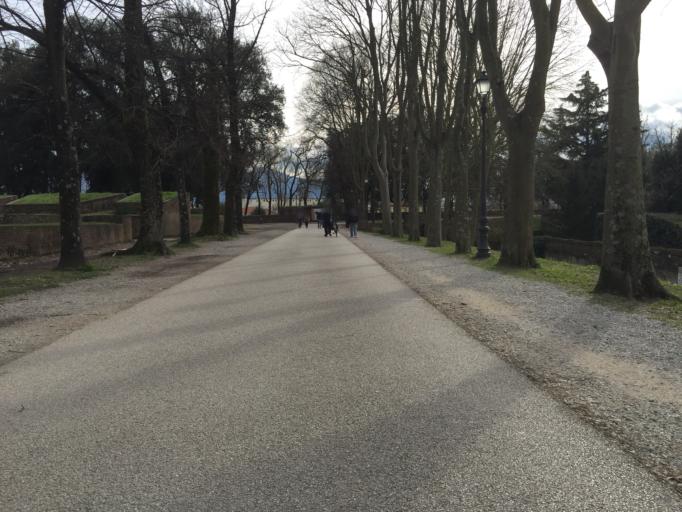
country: IT
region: Tuscany
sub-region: Provincia di Lucca
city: Lucca
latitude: 43.8423
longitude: 10.5138
